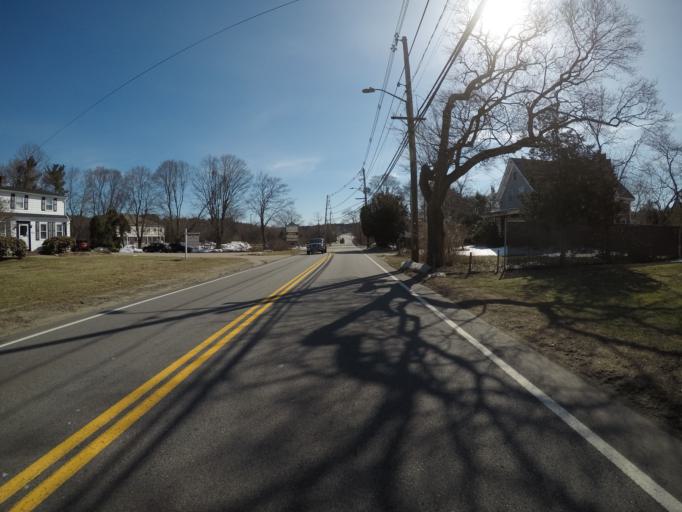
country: US
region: Massachusetts
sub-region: Bristol County
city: Easton
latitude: 42.0239
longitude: -71.1260
